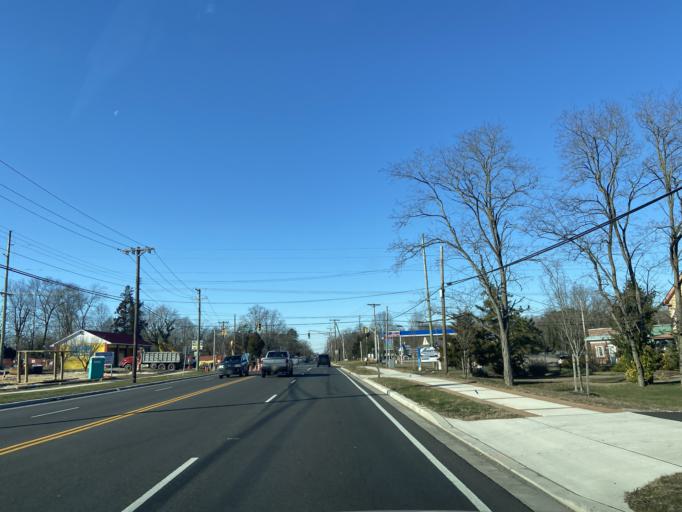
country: US
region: New Jersey
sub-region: Cumberland County
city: Vineland
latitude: 39.4875
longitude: -75.0515
